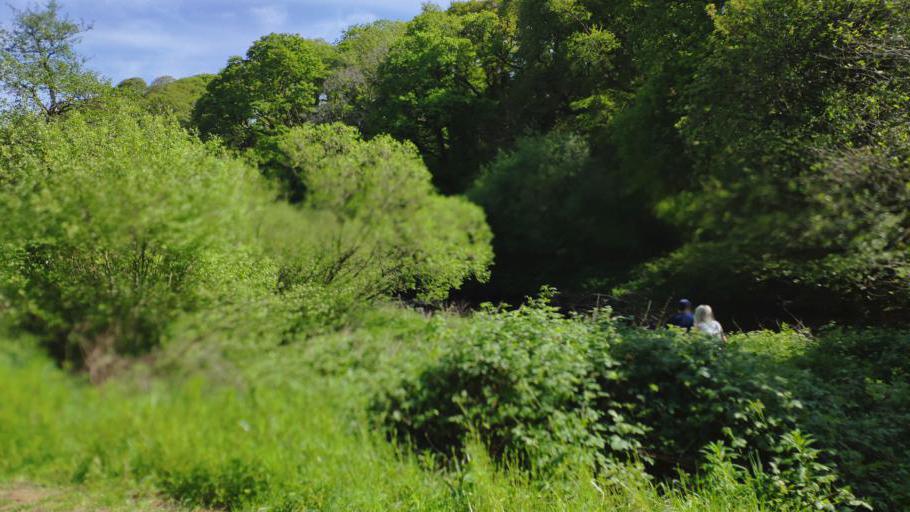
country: IE
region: Munster
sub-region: County Cork
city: Blarney
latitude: 51.9438
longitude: -8.5658
